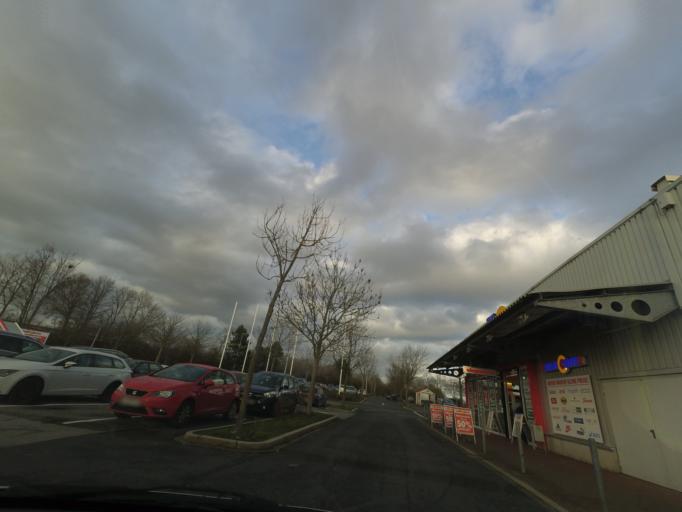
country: DE
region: North Rhine-Westphalia
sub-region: Regierungsbezirk Dusseldorf
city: Grevenbroich
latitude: 51.1090
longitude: 6.5786
